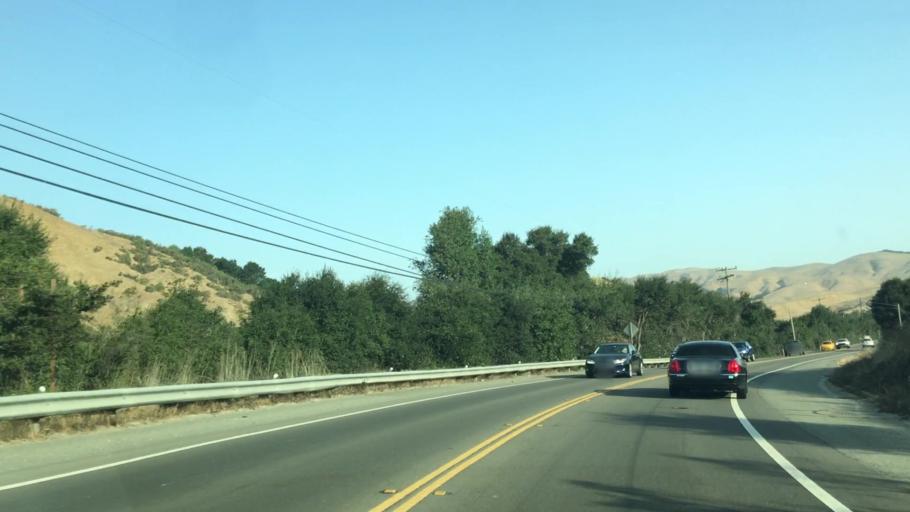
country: US
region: California
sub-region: Contra Costa County
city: San Ramon
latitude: 37.7537
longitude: -122.0297
